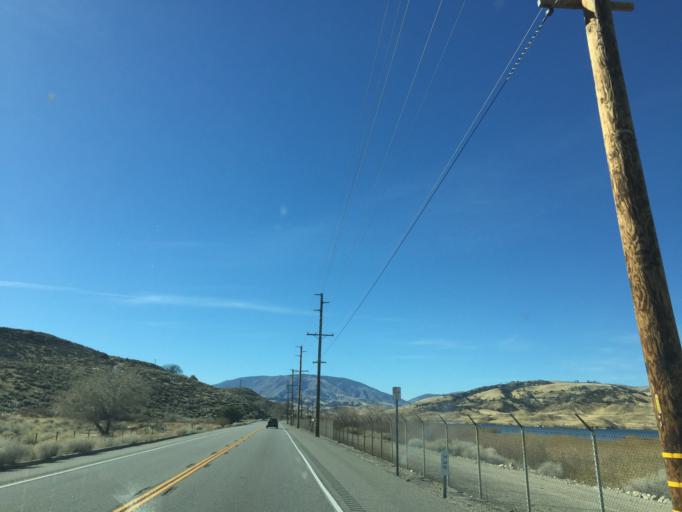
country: US
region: California
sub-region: Kern County
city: Lebec
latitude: 34.7684
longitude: -118.7406
